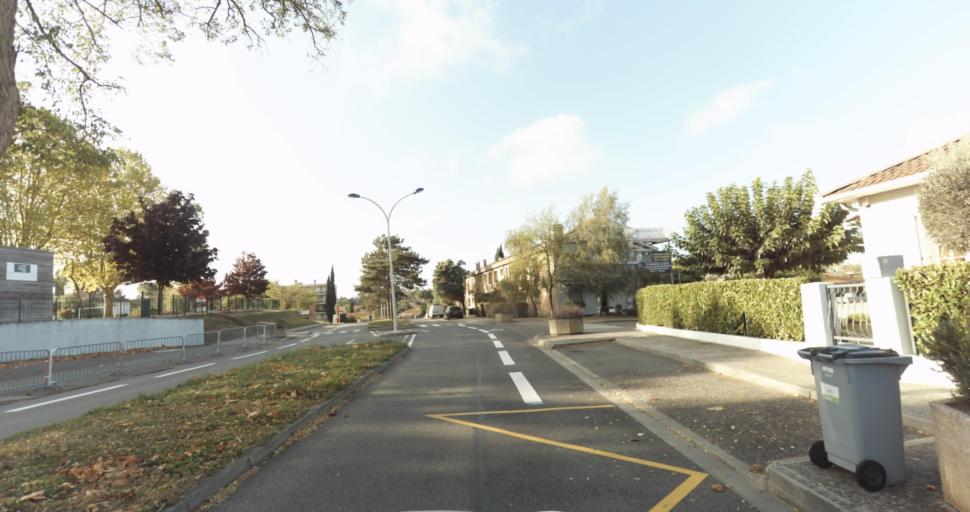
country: FR
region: Midi-Pyrenees
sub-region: Departement de la Haute-Garonne
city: Ramonville-Saint-Agne
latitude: 43.5445
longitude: 1.4638
